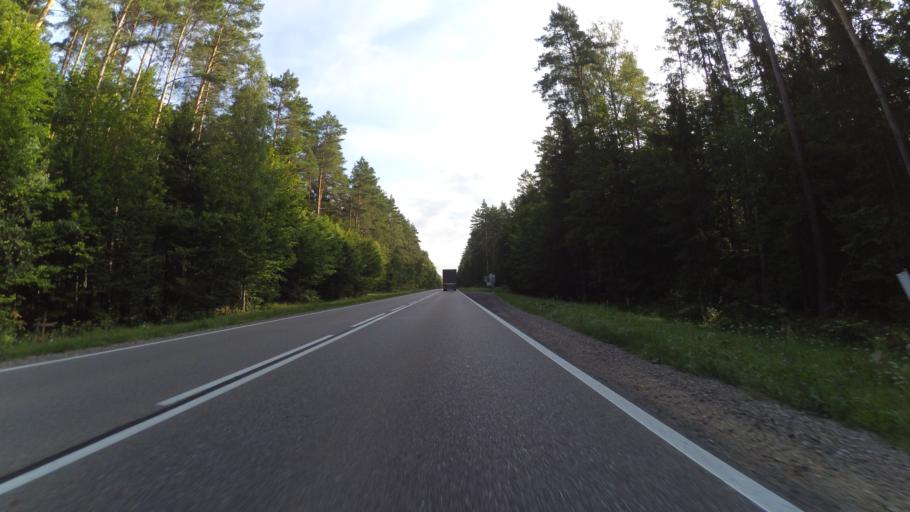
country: PL
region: Podlasie
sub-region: Powiat bialostocki
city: Czarna Bialostocka
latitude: 53.2629
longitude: 23.2573
